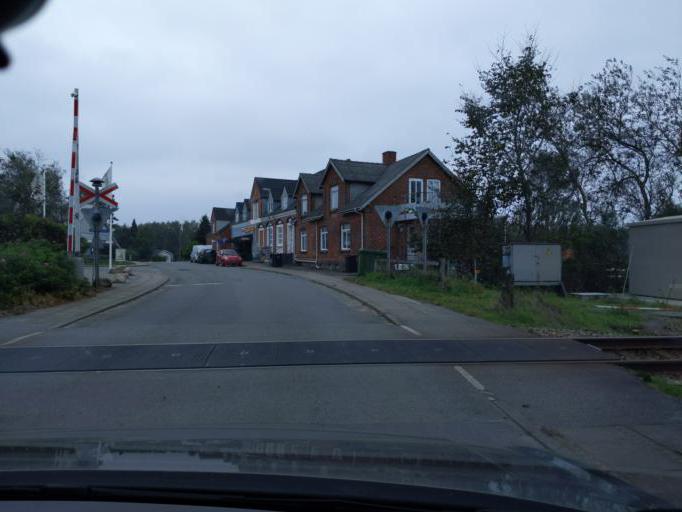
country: DK
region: Central Jutland
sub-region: Viborg Kommune
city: Stoholm
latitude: 56.4751
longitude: 9.2288
